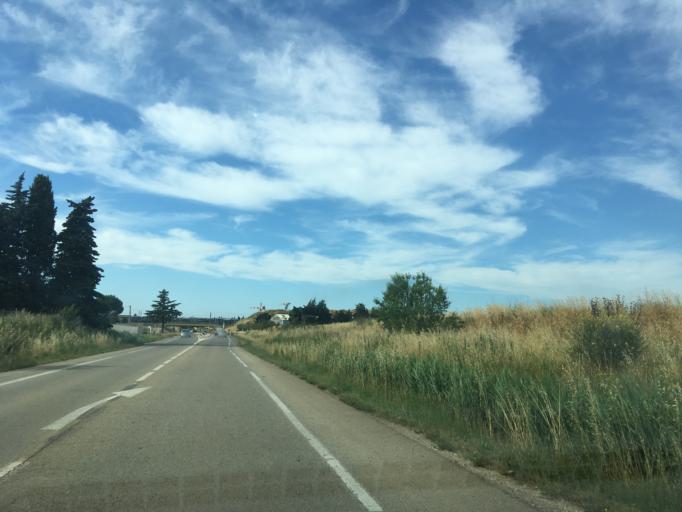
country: FR
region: Languedoc-Roussillon
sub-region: Departement du Gard
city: Garons
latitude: 43.7829
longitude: 4.4300
